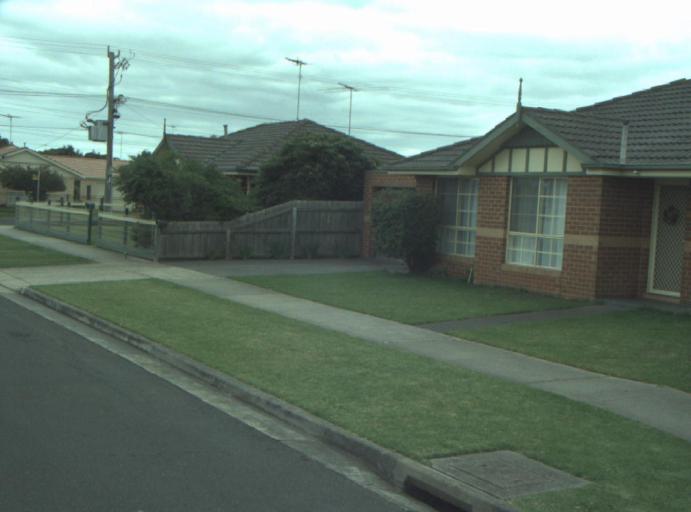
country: AU
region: Victoria
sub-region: Greater Geelong
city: Breakwater
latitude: -38.1958
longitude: 144.3367
